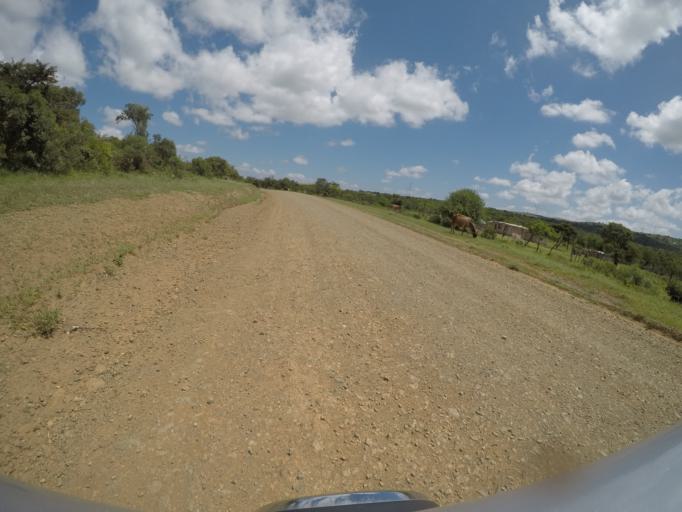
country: ZA
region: KwaZulu-Natal
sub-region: uThungulu District Municipality
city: Empangeni
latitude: -28.5952
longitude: 31.8305
